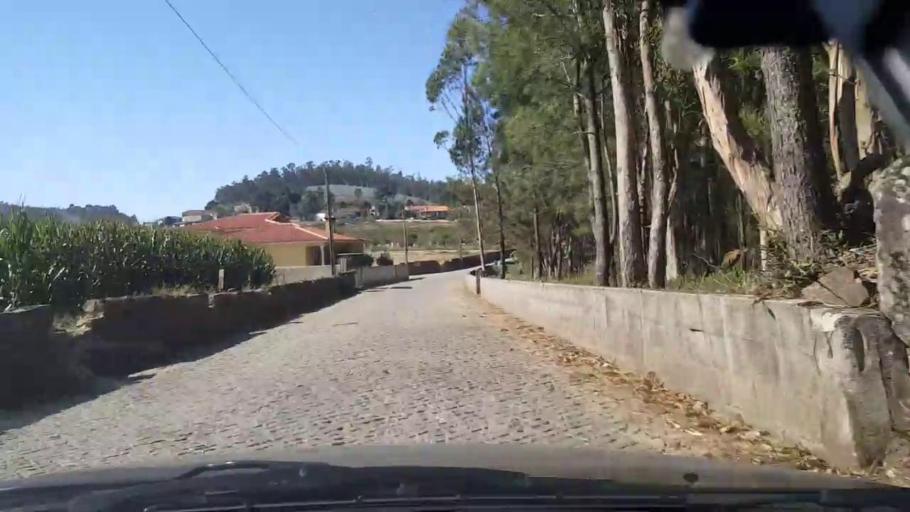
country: PT
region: Braga
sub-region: Vila Nova de Famalicao
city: Ribeirao
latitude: 41.3800
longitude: -8.6391
